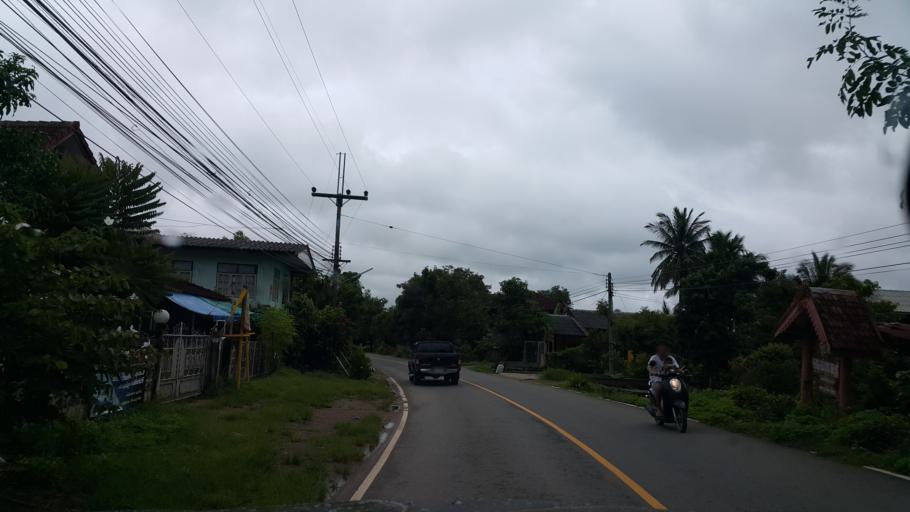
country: TH
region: Phayao
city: Chiang Kham
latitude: 19.5232
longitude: 100.3491
